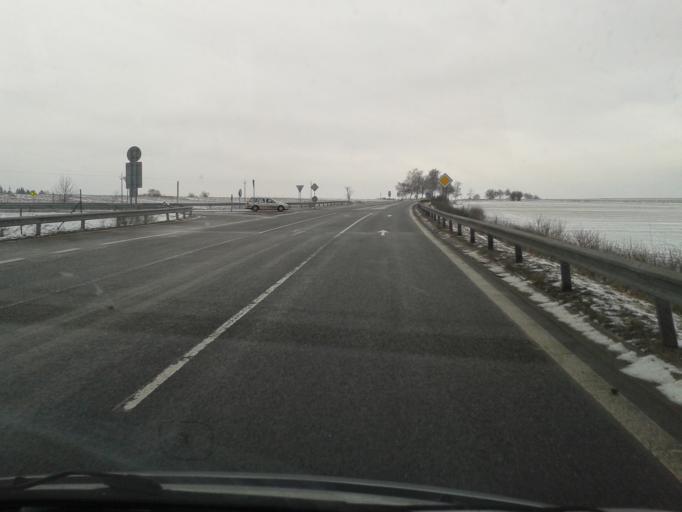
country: SK
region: Zilinsky
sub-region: Okres Zilina
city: Trstena
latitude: 49.3780
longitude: 19.6306
